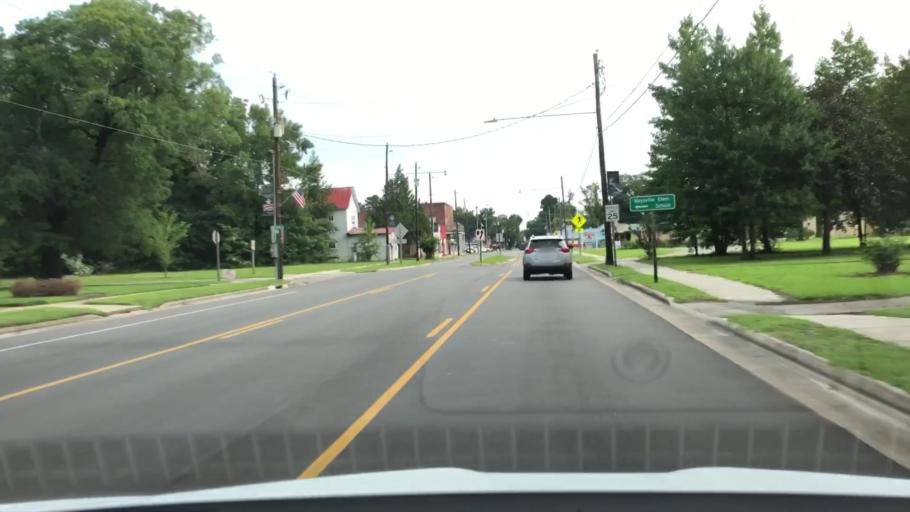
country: US
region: North Carolina
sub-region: Jones County
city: Maysville
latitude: 34.9035
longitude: -77.2315
